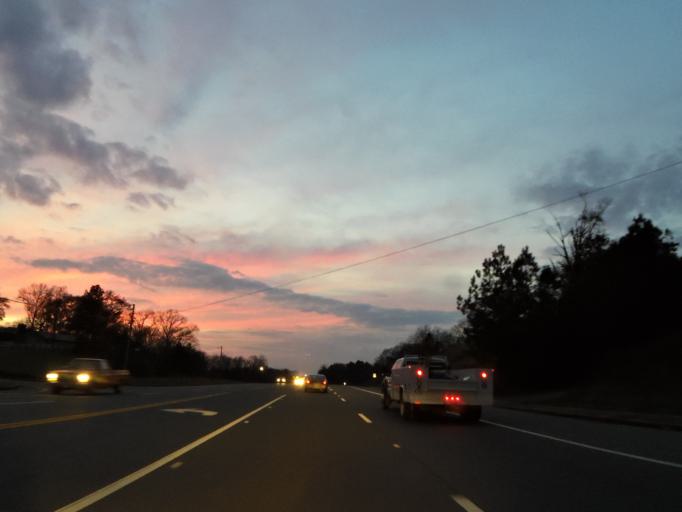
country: US
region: Tennessee
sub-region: Polk County
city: Benton
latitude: 35.1675
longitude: -84.6611
